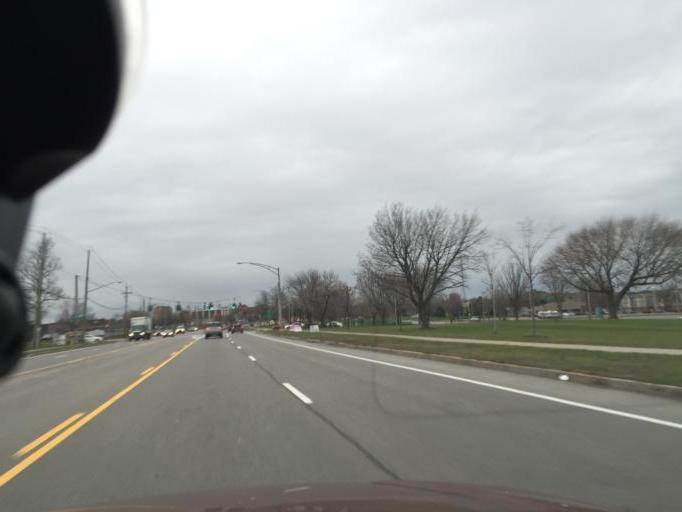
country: US
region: New York
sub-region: Monroe County
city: Rochester
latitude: 43.1018
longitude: -77.6147
